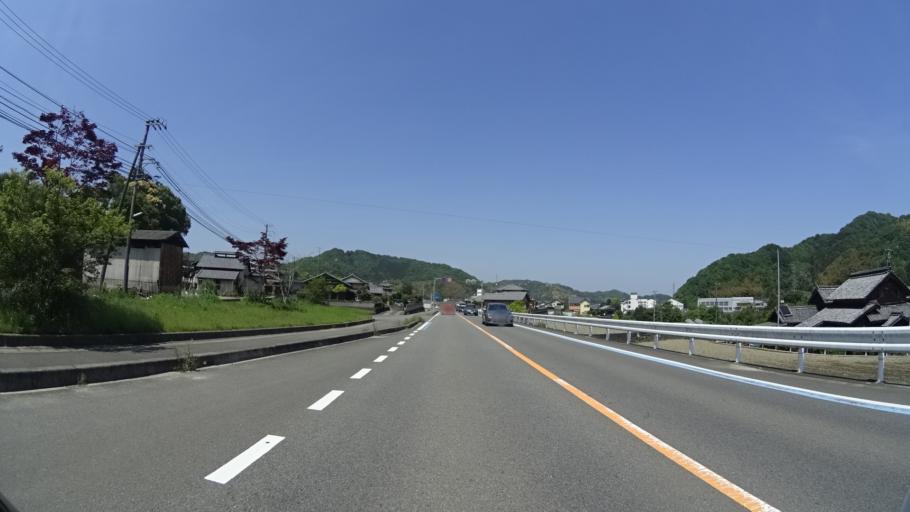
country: JP
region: Ehime
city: Hojo
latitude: 34.0155
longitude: 132.9396
